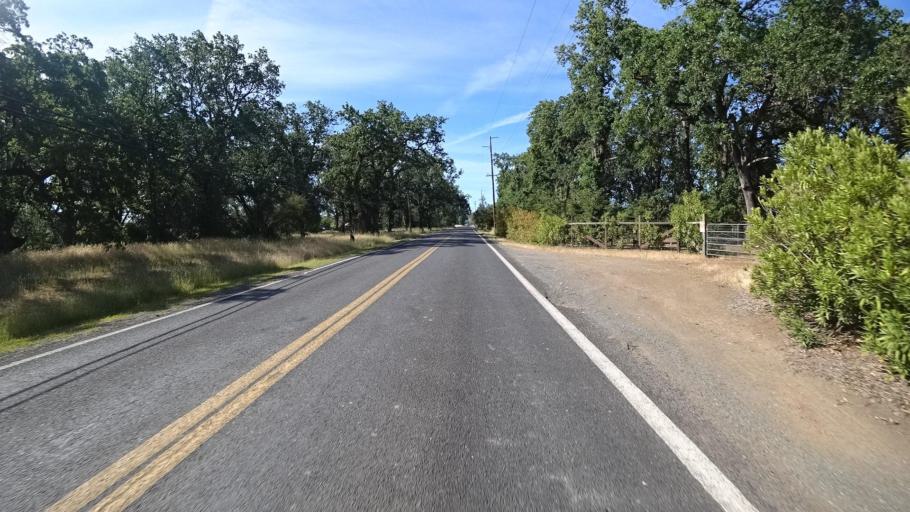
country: US
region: California
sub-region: Lake County
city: Lakeport
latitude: 38.9992
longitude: -122.8941
